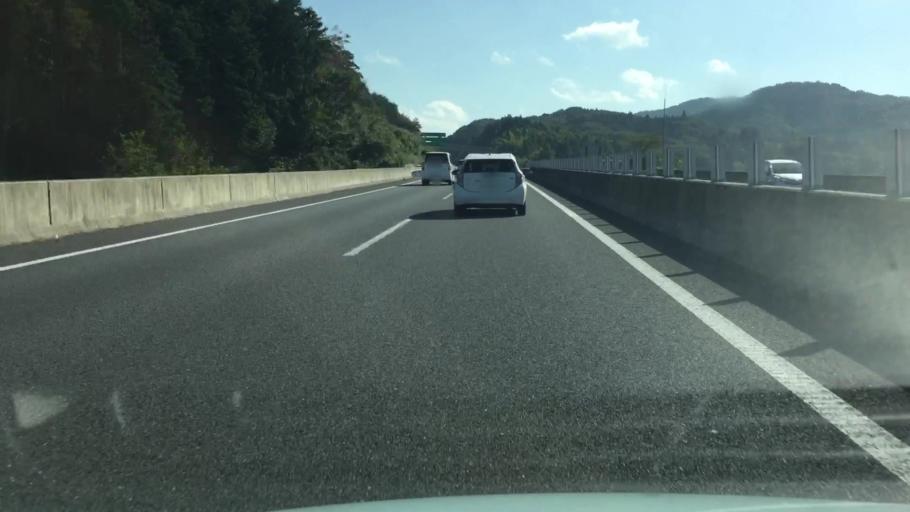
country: JP
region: Ibaraki
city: Kasama
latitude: 36.3426
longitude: 140.1889
